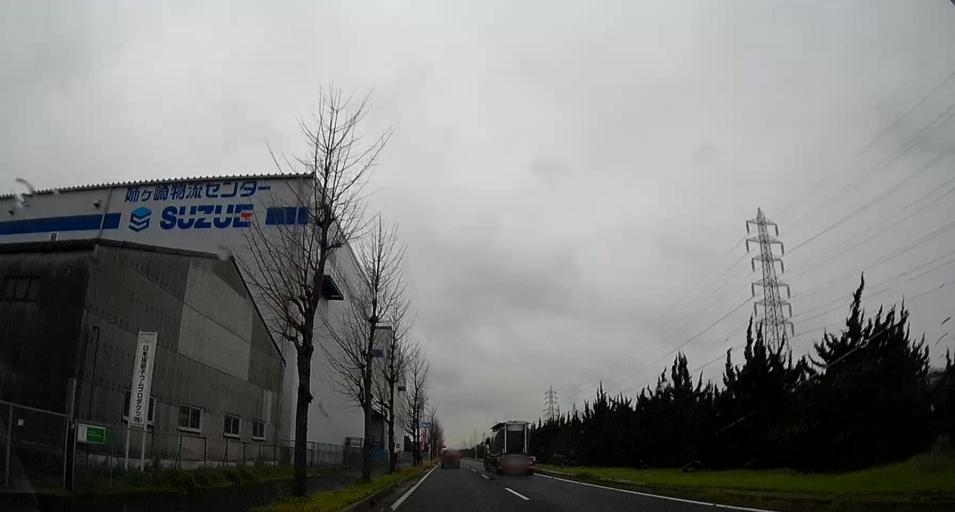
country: JP
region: Chiba
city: Ichihara
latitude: 35.4986
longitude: 140.0482
